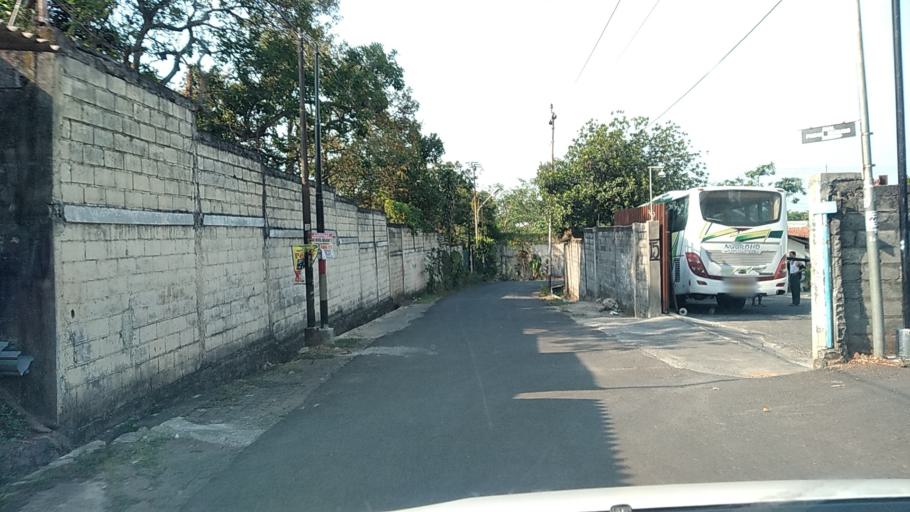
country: ID
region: Central Java
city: Semarang
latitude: -7.0662
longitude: 110.4259
